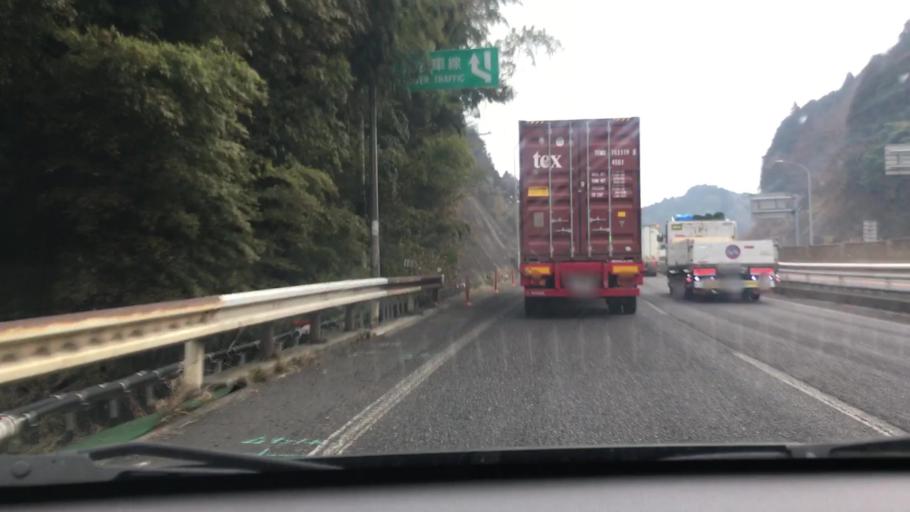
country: JP
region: Mie
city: Ueno-ebisumachi
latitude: 34.8395
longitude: 136.2646
